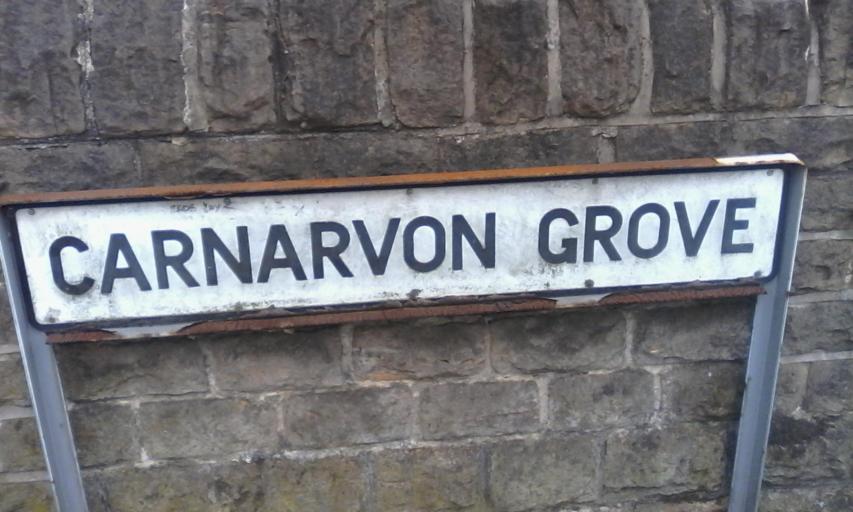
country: GB
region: England
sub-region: Nottinghamshire
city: Arnold
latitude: 52.9709
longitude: -1.0954
